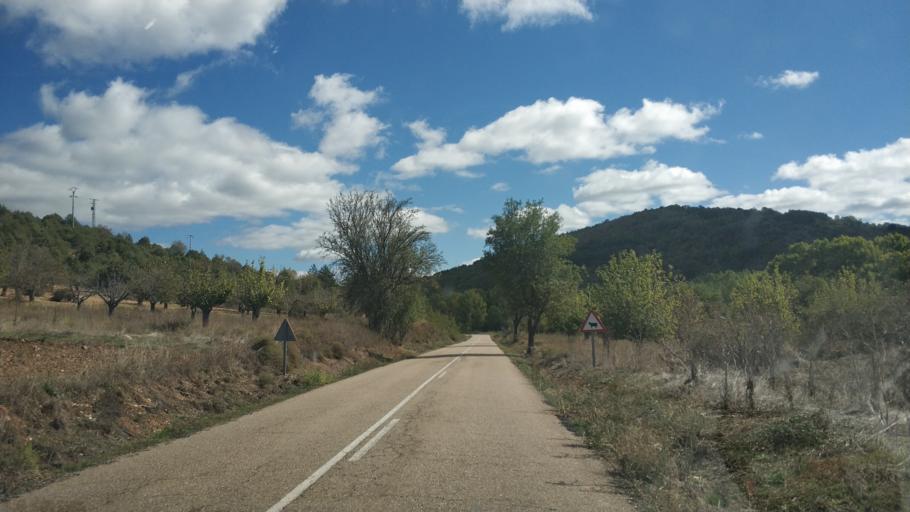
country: ES
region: Castille and Leon
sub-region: Provincia de Burgos
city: Covarrubias
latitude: 42.0557
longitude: -3.5108
